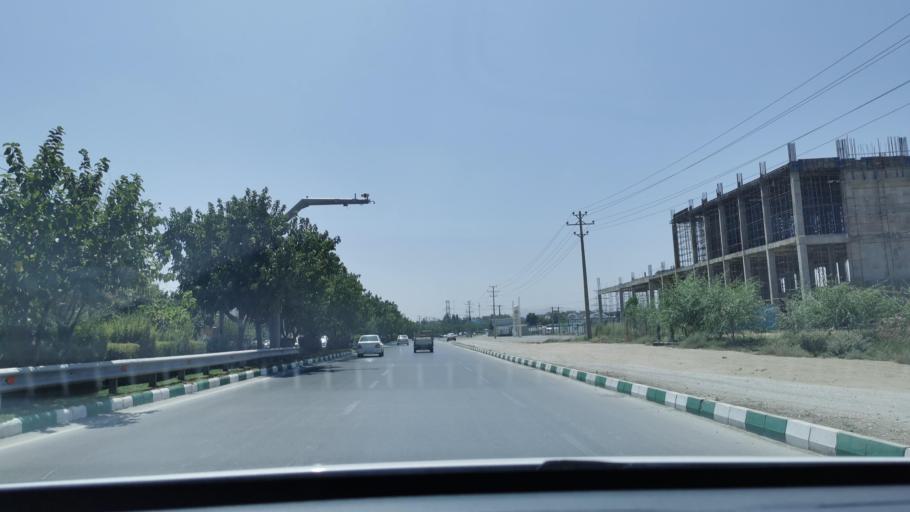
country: IR
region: Razavi Khorasan
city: Mashhad
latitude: 36.3541
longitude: 59.6309
